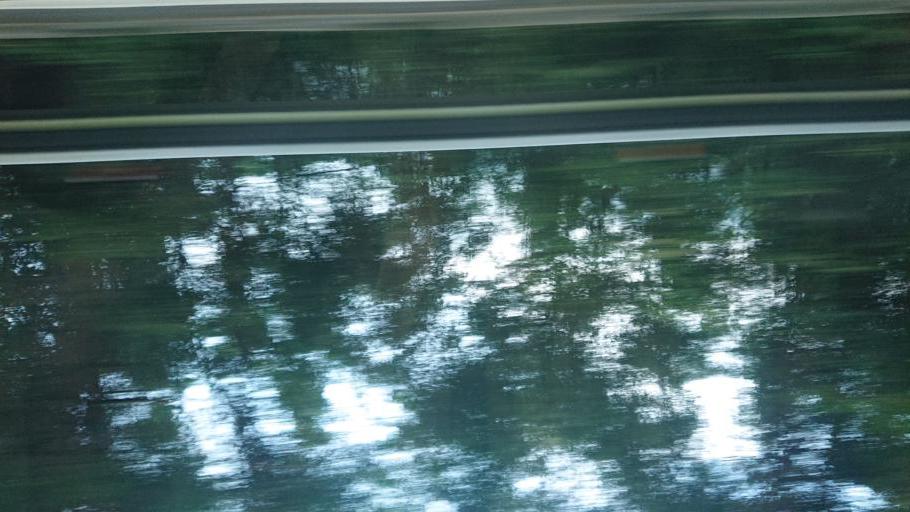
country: TW
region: Taiwan
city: Lugu
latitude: 23.4832
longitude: 120.7466
